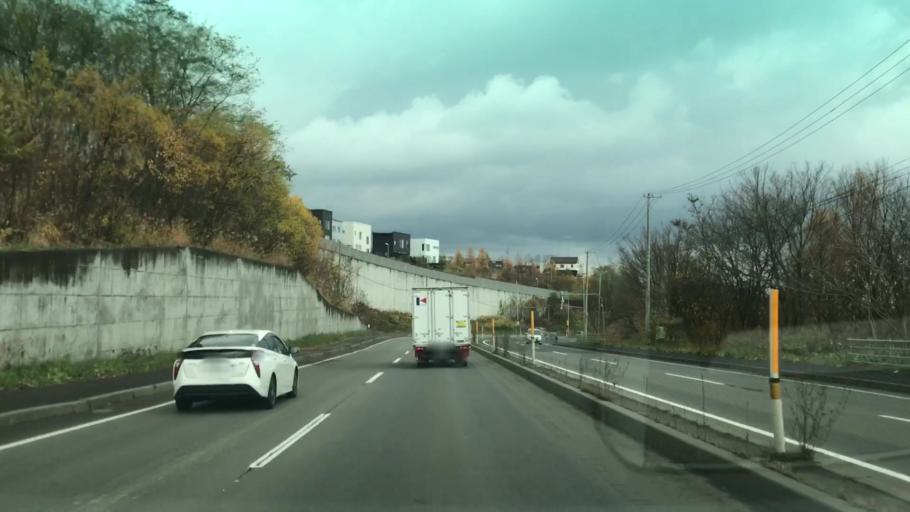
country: JP
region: Hokkaido
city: Otaru
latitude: 43.1721
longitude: 141.0715
